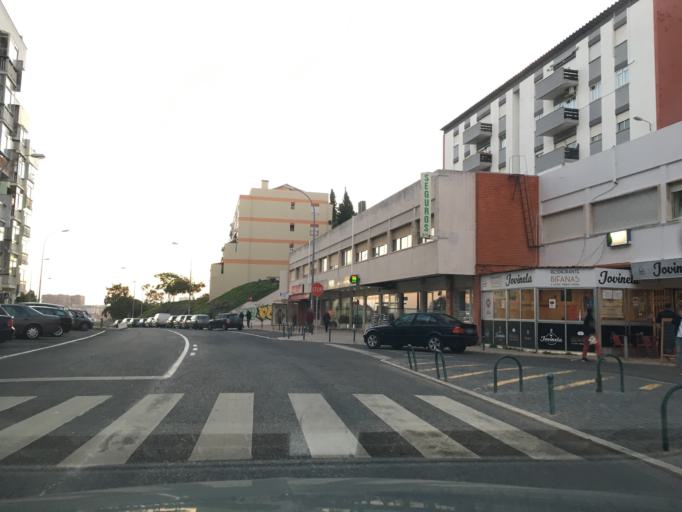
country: PT
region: Lisbon
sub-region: Oeiras
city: Oeiras
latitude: 38.6958
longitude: -9.3094
